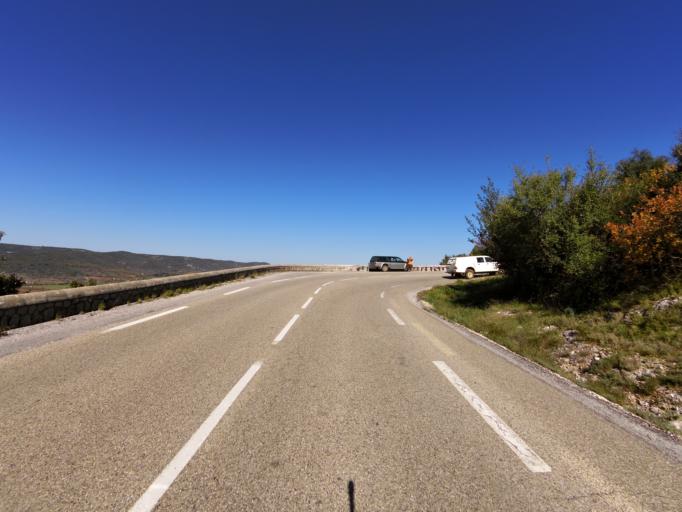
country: FR
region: Rhone-Alpes
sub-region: Departement de l'Ardeche
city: Ruoms
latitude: 44.4096
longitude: 4.4184
